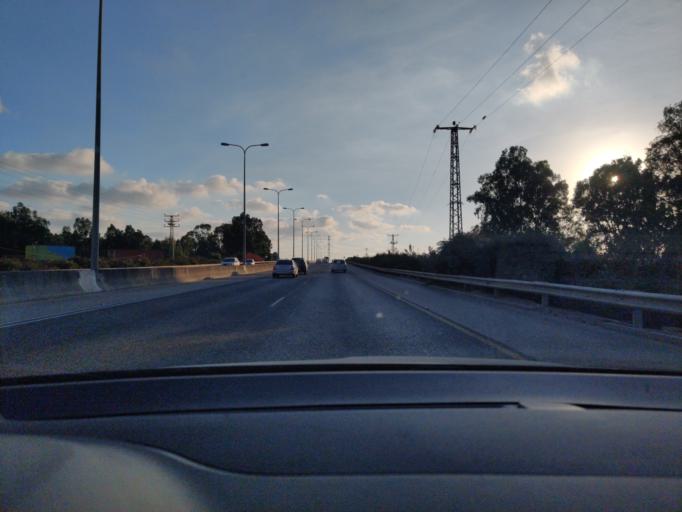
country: IL
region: Central District
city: Elyakhin
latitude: 32.4470
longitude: 34.9530
